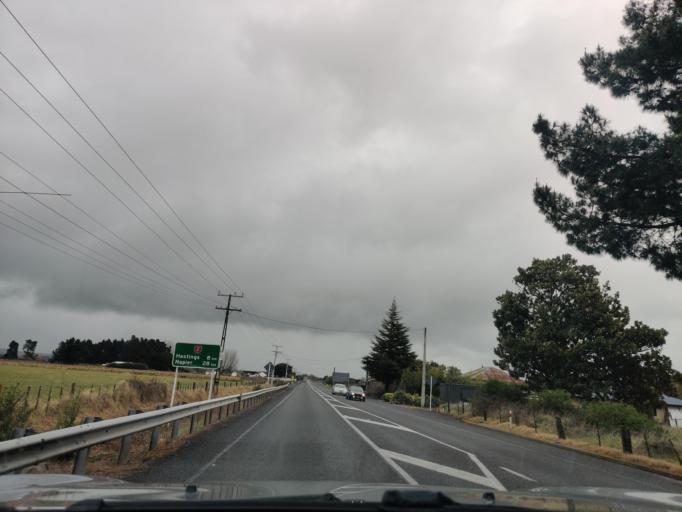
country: NZ
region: Hawke's Bay
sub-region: Hastings District
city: Hastings
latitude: -39.6903
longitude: 176.7913
